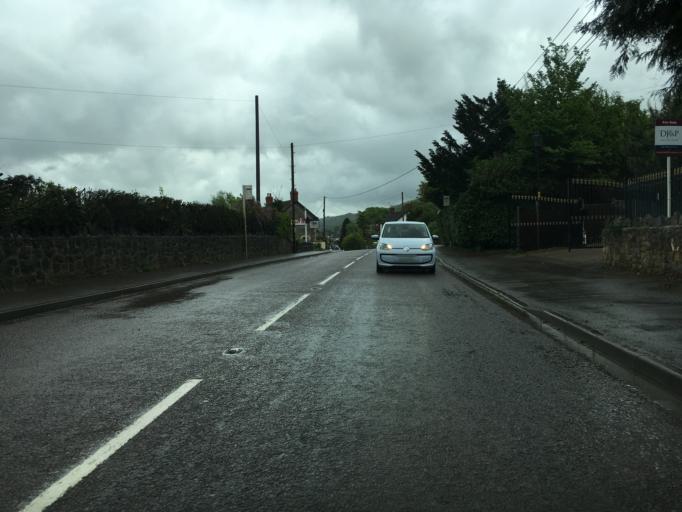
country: GB
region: England
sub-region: North Somerset
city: Sandford
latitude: 51.3330
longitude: -2.8356
